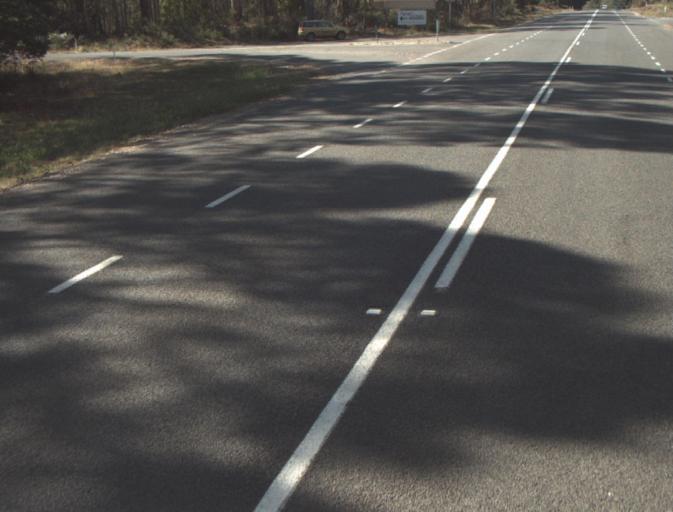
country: AU
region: Tasmania
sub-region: Launceston
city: Mayfield
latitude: -41.3127
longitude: 147.1980
